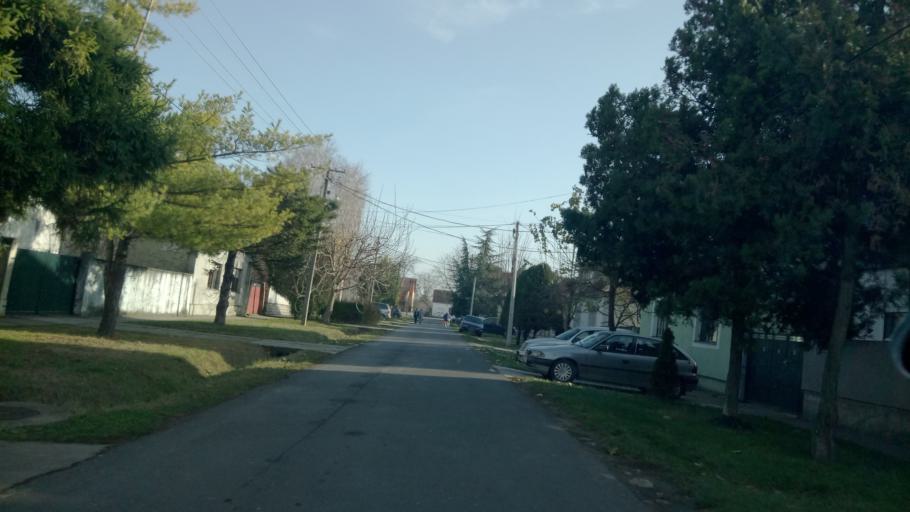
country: RS
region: Autonomna Pokrajina Vojvodina
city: Nova Pazova
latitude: 44.9501
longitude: 20.2195
